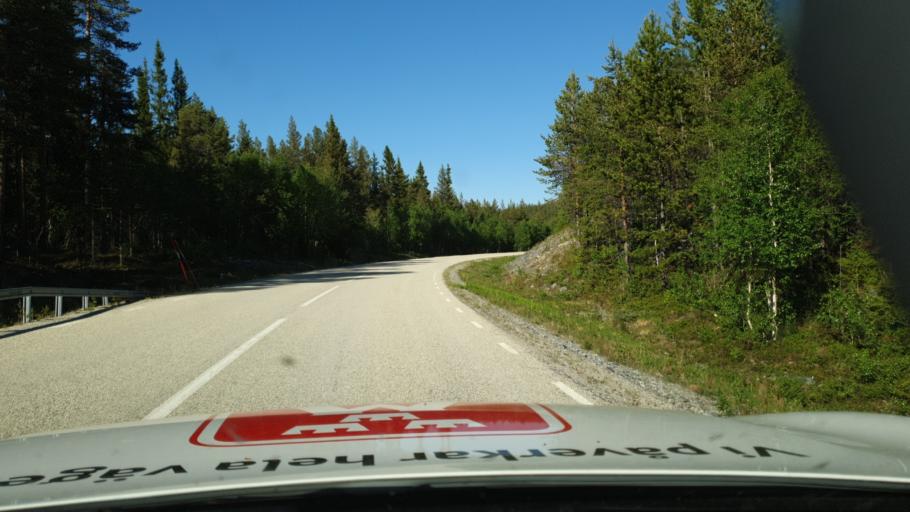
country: SE
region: Jaemtland
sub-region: Are Kommun
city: Are
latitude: 62.8427
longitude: 13.1586
